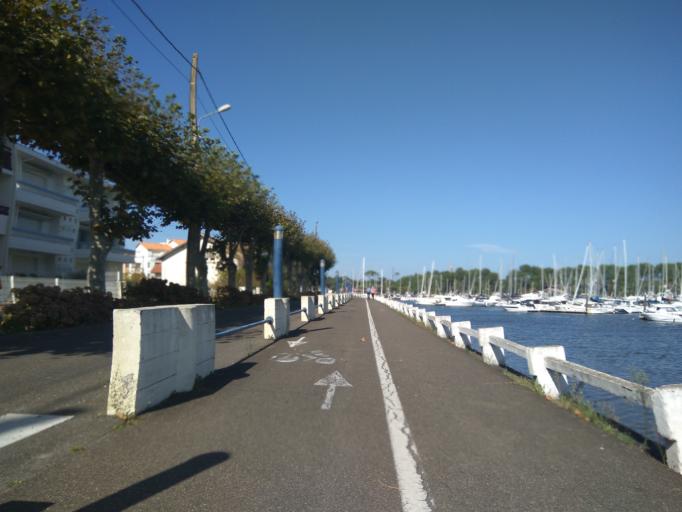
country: FR
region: Aquitaine
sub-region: Departement des Landes
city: Capbreton
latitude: 43.6499
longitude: -1.4360
